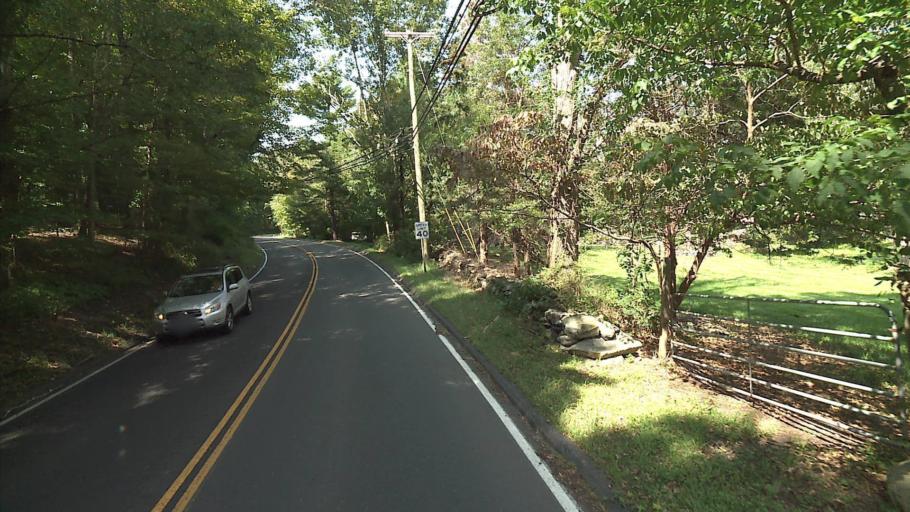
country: US
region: Connecticut
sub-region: Fairfield County
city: Georgetown
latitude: 41.2670
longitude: -73.3300
